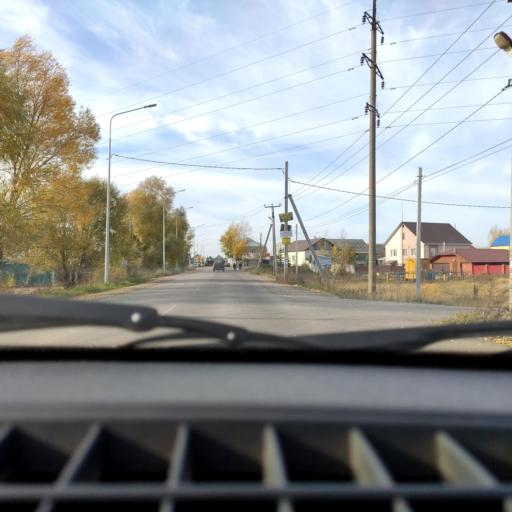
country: RU
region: Bashkortostan
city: Ufa
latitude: 54.6381
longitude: 55.9244
